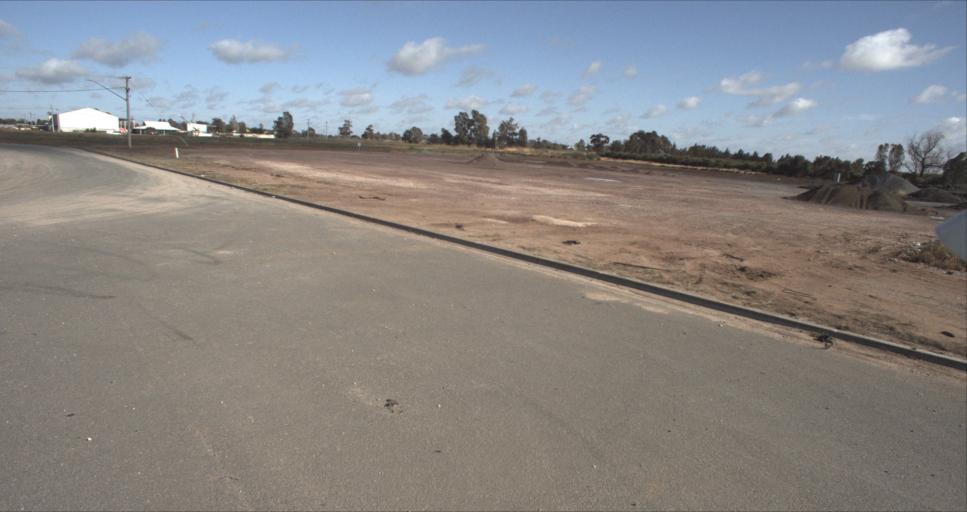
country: AU
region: New South Wales
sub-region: Leeton
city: Leeton
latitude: -34.5455
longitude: 146.3924
